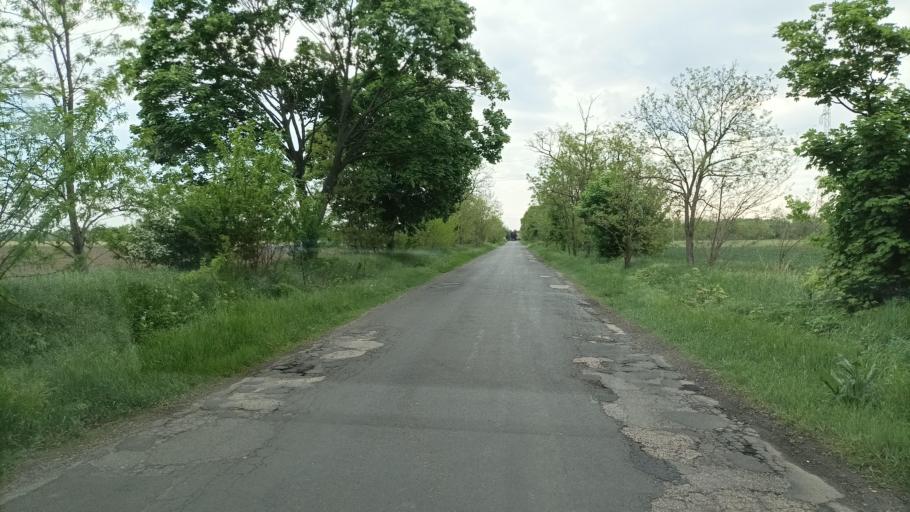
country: HU
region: Pest
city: Nyaregyhaza
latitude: 47.2709
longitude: 19.5195
